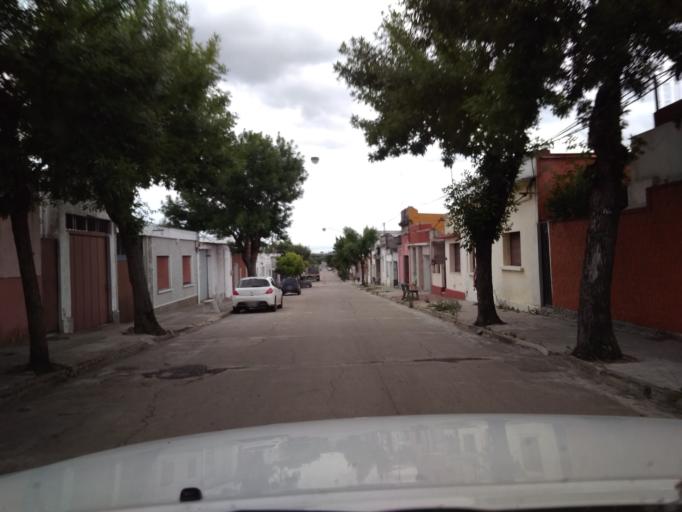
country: UY
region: Florida
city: Florida
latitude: -34.0983
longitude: -56.2124
